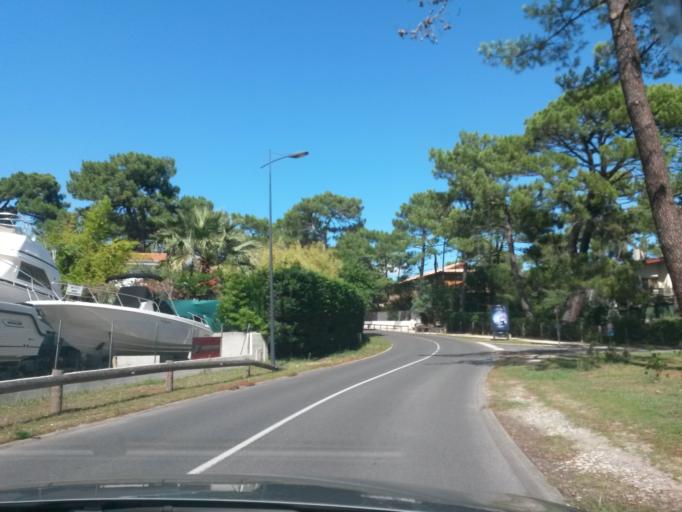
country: FR
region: Aquitaine
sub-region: Departement de la Gironde
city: Arcachon
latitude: 44.6587
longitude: -1.2445
